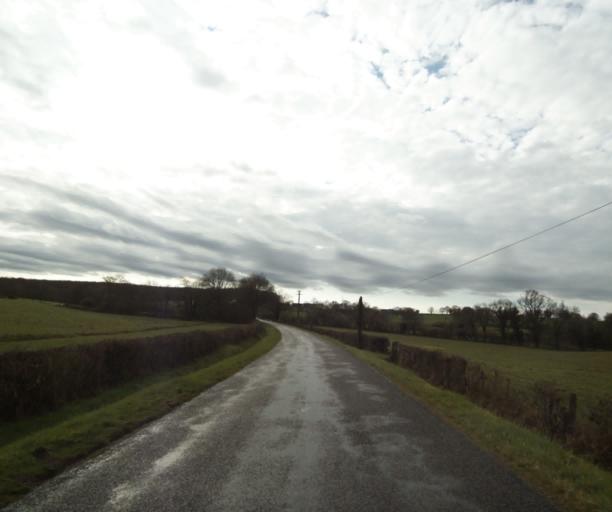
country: FR
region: Auvergne
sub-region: Departement de l'Allier
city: Toulon-sur-Allier
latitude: 46.5255
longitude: 3.4127
